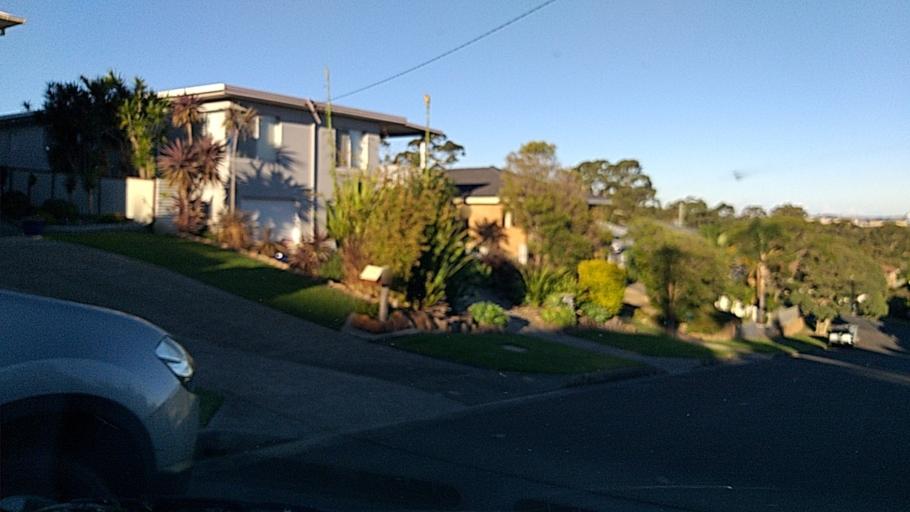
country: AU
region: New South Wales
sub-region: Wollongong
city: Cordeaux Heights
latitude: -34.4285
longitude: 150.8440
